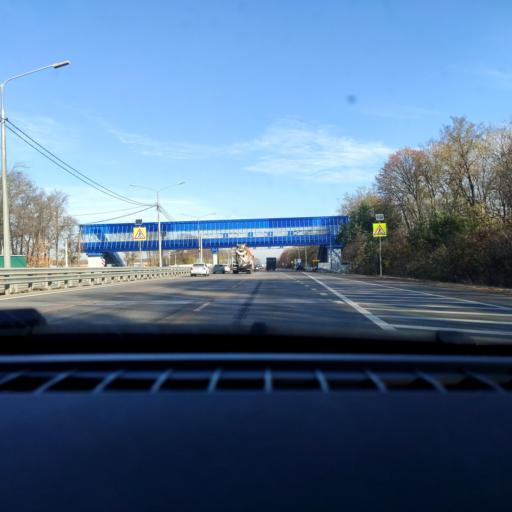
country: RU
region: Voronezj
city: Podgornoye
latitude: 51.8049
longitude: 39.2042
